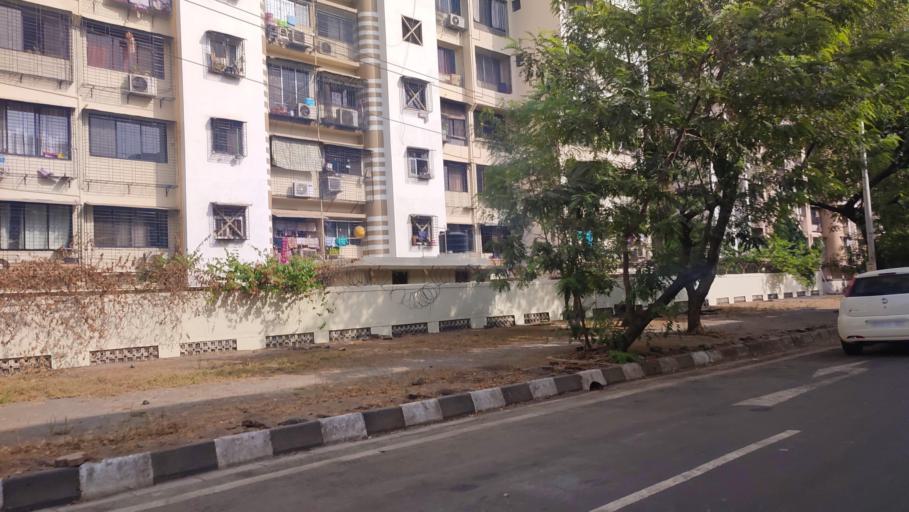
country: IN
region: Maharashtra
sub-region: Thane
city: Thane
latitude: 19.1667
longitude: 72.9654
